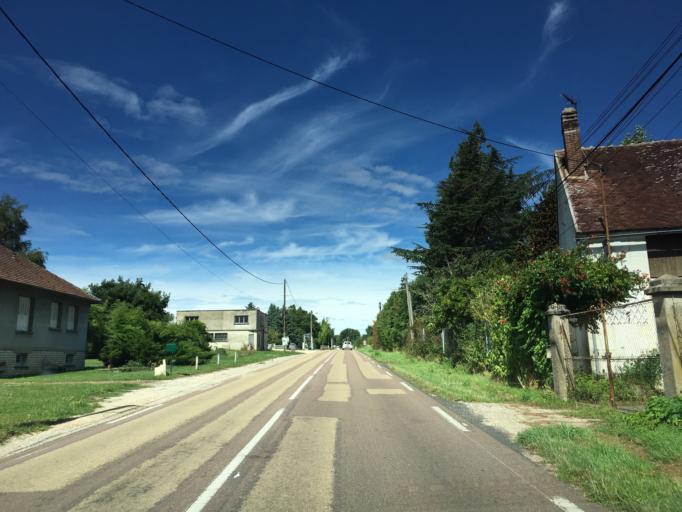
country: FR
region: Bourgogne
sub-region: Departement de l'Yonne
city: Charbuy
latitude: 47.8159
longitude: 3.4616
